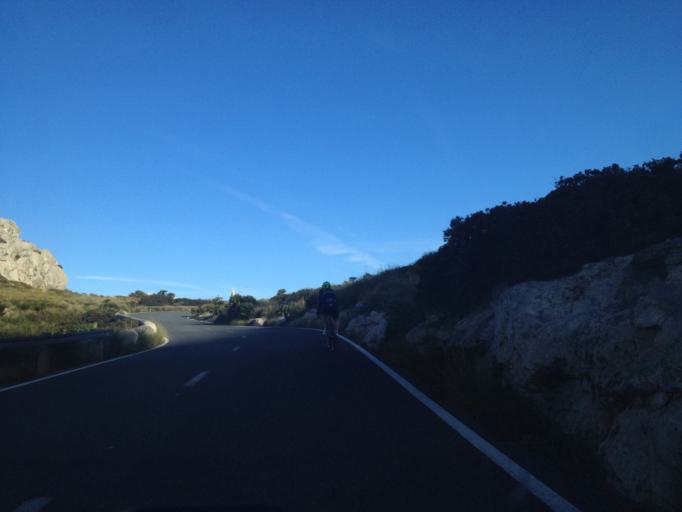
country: ES
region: Balearic Islands
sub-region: Illes Balears
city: Alcudia
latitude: 39.9278
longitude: 3.1099
